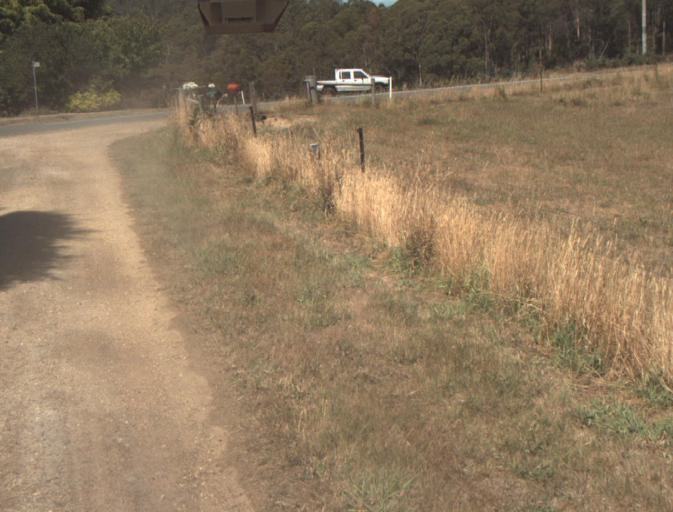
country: AU
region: Tasmania
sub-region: Launceston
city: Mayfield
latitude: -41.2725
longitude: 147.1275
